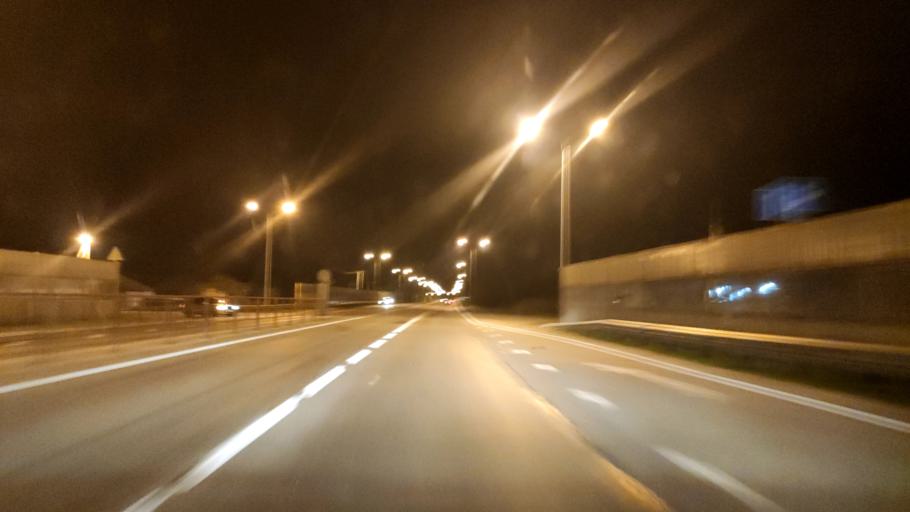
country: RU
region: Belgorod
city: Staryy Oskol
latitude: 51.3431
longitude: 37.8080
